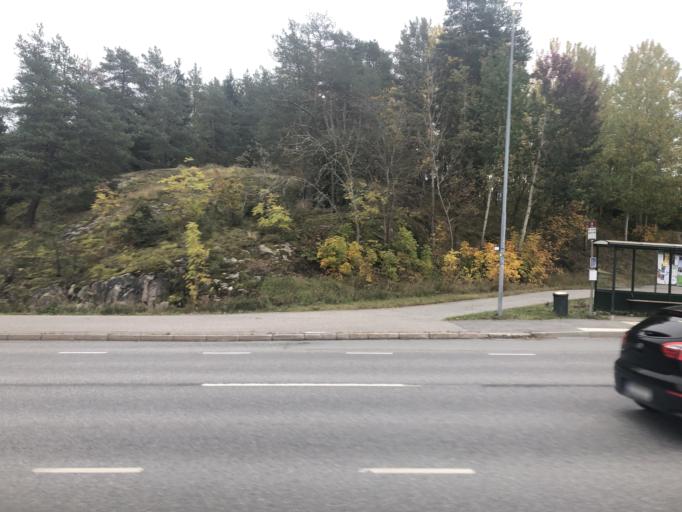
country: SE
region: Stockholm
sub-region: Jarfalla Kommun
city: Jakobsberg
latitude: 59.4177
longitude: 17.8131
